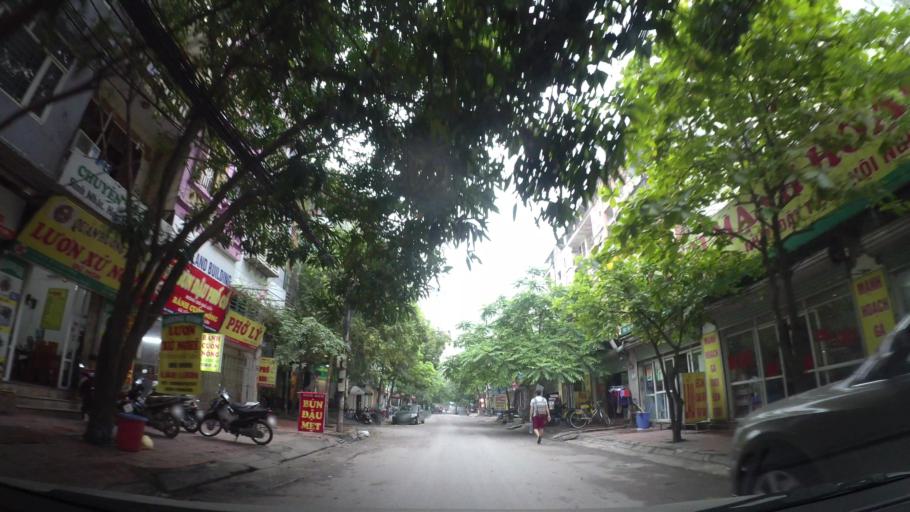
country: VN
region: Ha Noi
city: Cau Giay
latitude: 21.0316
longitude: 105.7853
